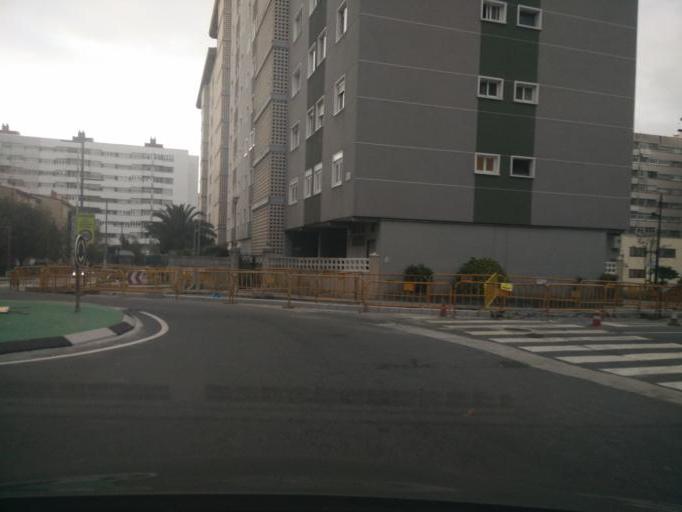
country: ES
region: Galicia
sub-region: Provincia da Coruna
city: A Coruna
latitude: 43.3441
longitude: -8.4135
